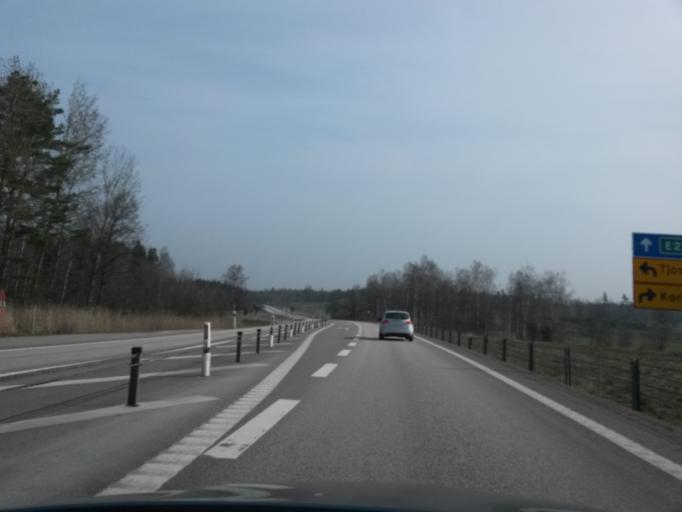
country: SE
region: Vaestra Goetaland
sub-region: Toreboda Kommun
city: Toereboda
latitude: 58.7648
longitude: 13.9797
